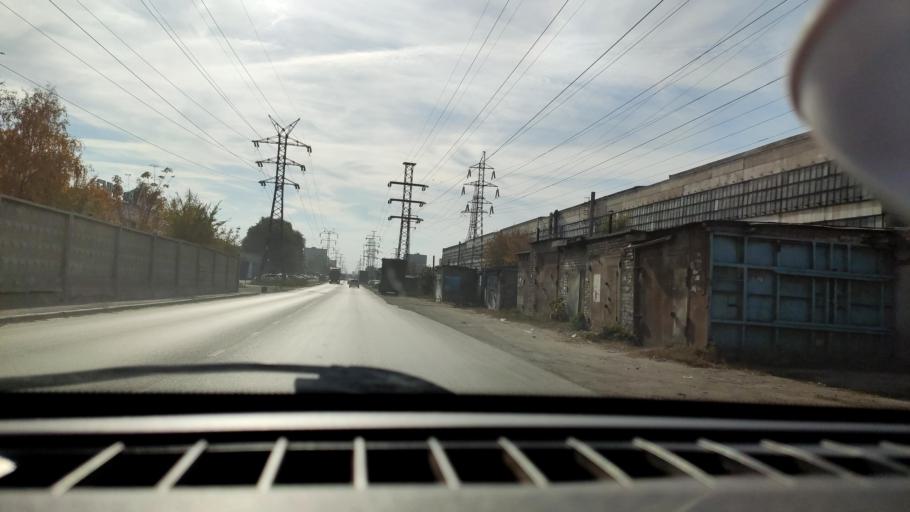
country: RU
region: Samara
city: Petra-Dubrava
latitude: 53.2441
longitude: 50.2914
